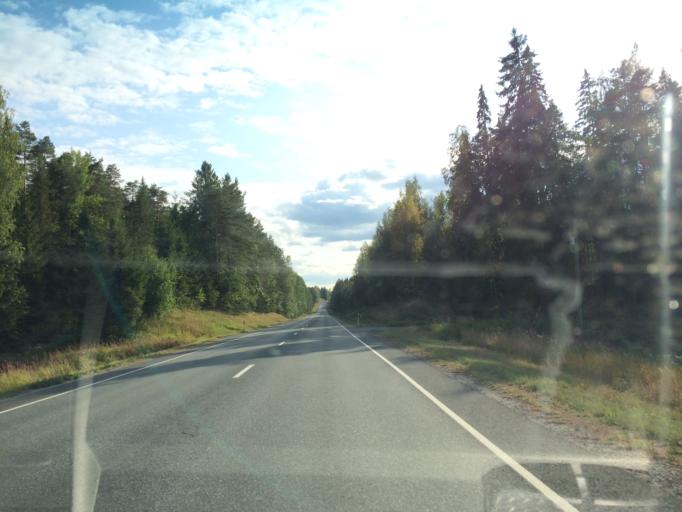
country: FI
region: Haeme
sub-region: Haemeenlinna
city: Haemeenlinna
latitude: 60.9467
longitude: 24.3967
